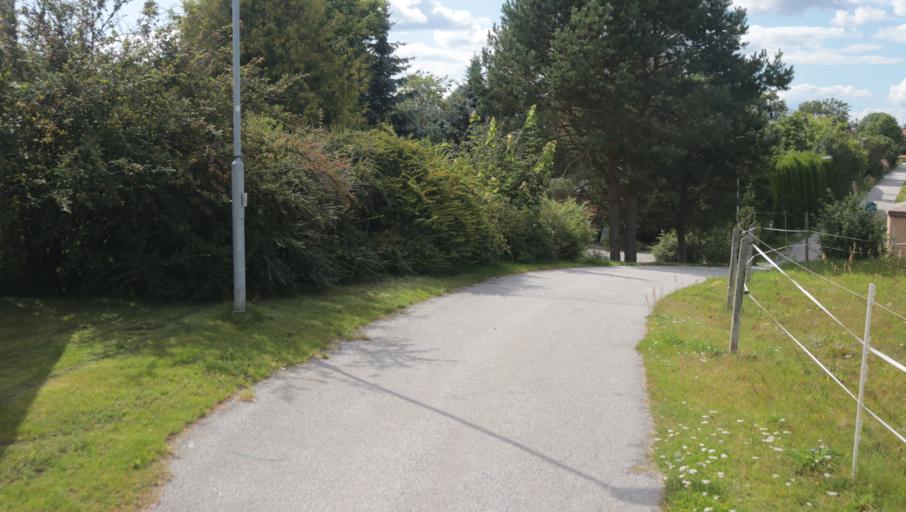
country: SE
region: Blekinge
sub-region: Karlshamns Kommun
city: Morrum
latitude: 56.1955
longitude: 14.7584
